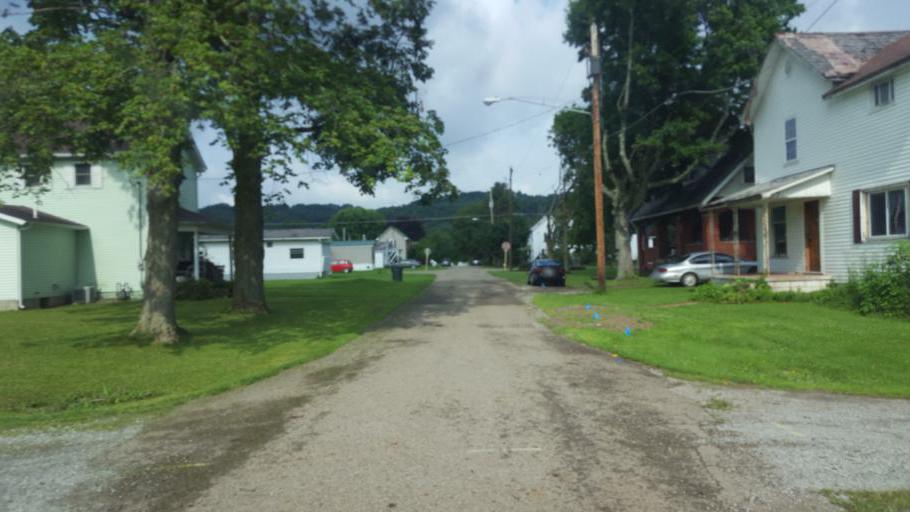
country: US
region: Ohio
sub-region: Columbiana County
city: Salineville
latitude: 40.5217
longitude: -80.8827
